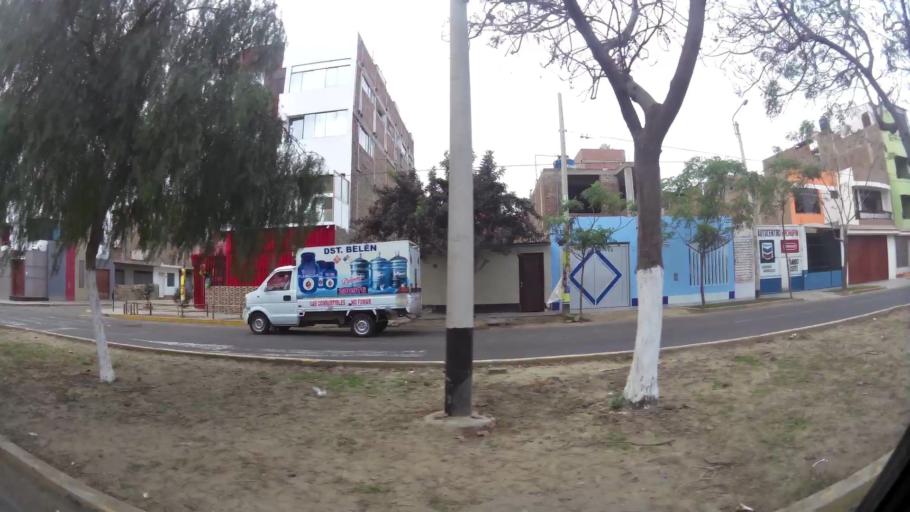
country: PE
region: La Libertad
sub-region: Provincia de Trujillo
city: Trujillo
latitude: -8.0990
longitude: -79.0227
